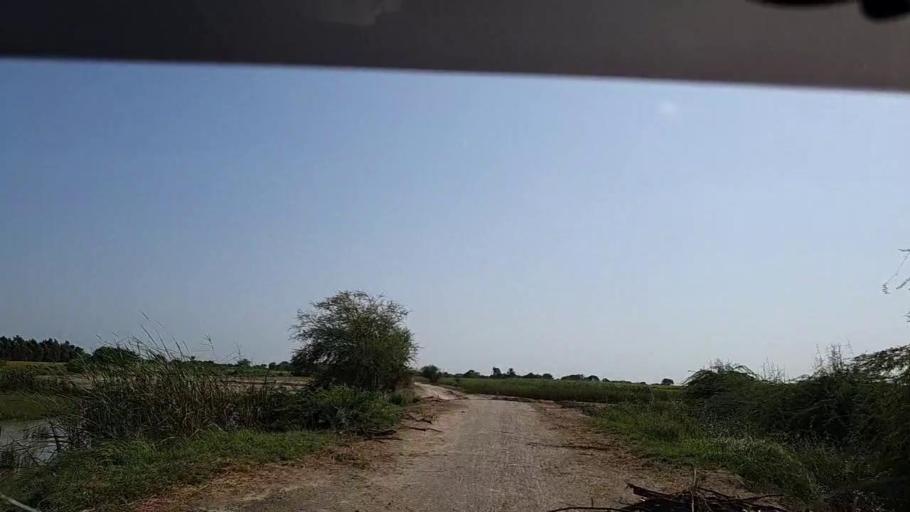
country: PK
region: Sindh
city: Badin
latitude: 24.6239
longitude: 68.7819
